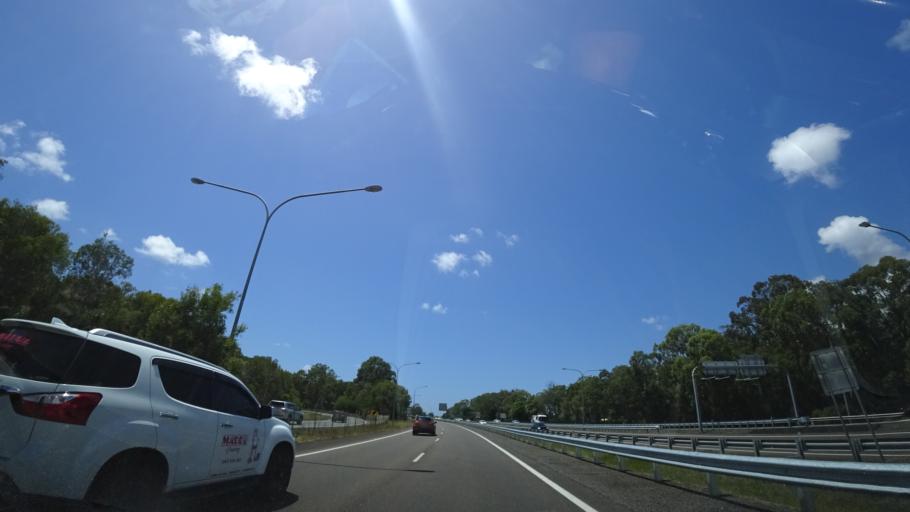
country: AU
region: Queensland
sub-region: Sunshine Coast
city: Mooloolaba
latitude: -26.6944
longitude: 153.1121
